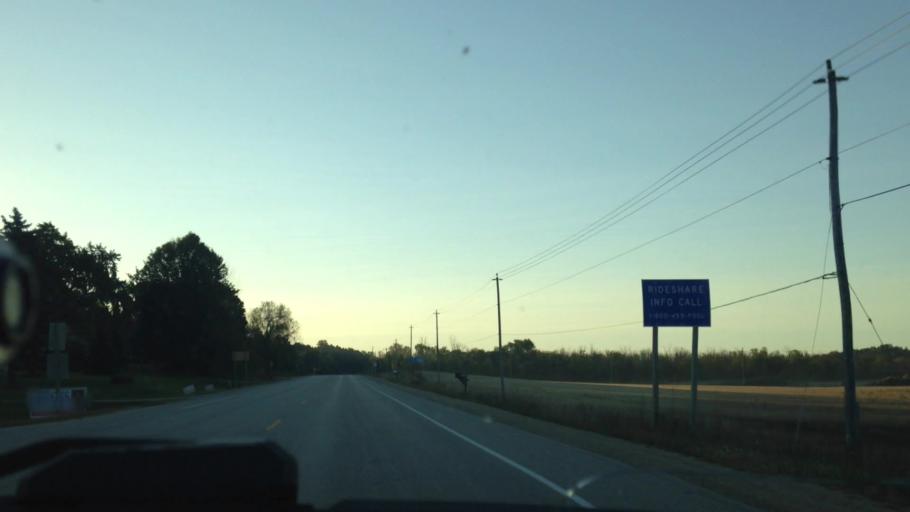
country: US
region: Wisconsin
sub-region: Washington County
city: Newburg
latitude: 43.4279
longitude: -88.0391
